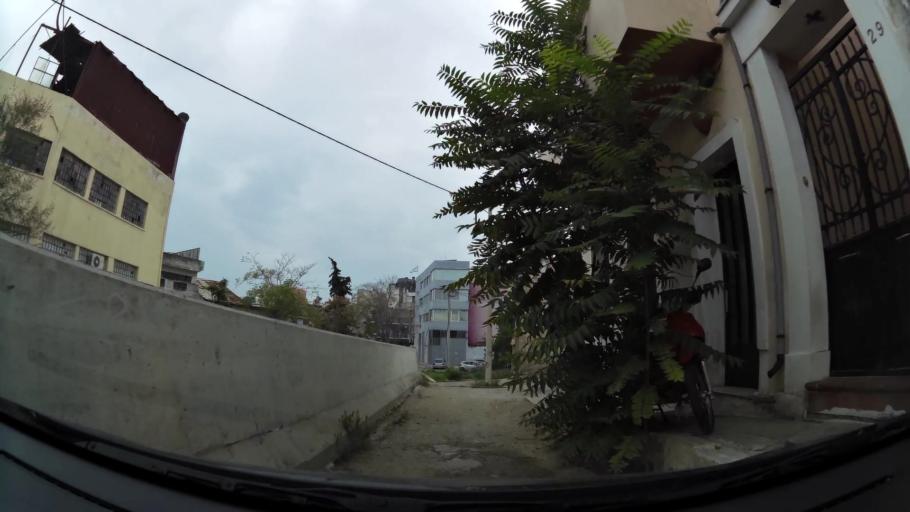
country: GR
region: Attica
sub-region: Nomos Attikis
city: Piraeus
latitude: 37.9530
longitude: 23.6369
